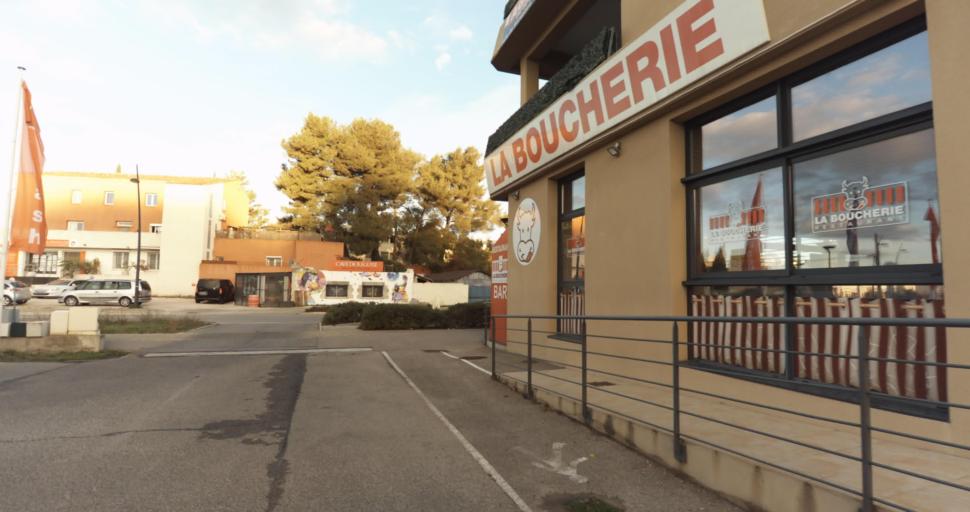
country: FR
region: Provence-Alpes-Cote d'Azur
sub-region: Departement des Bouches-du-Rhone
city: Venelles
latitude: 43.5830
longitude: 5.4734
